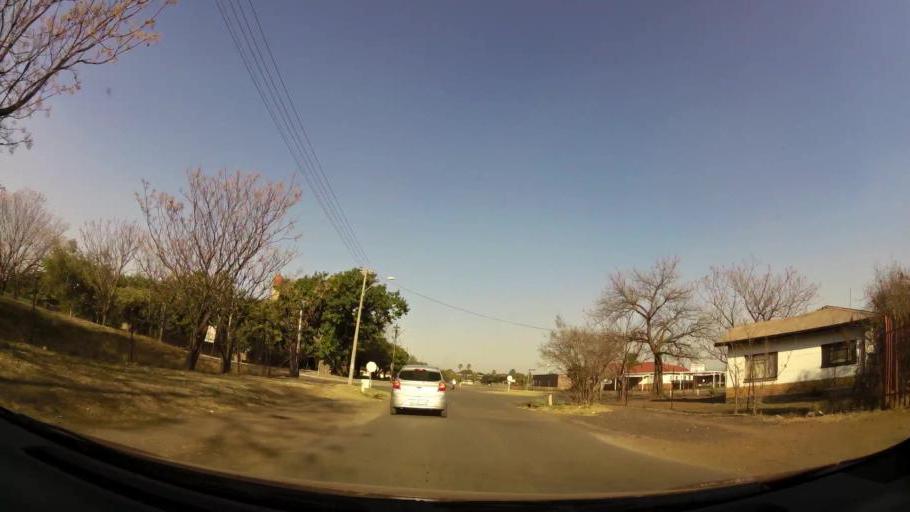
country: ZA
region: North-West
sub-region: Bojanala Platinum District Municipality
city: Rustenburg
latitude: -25.6475
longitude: 27.2403
